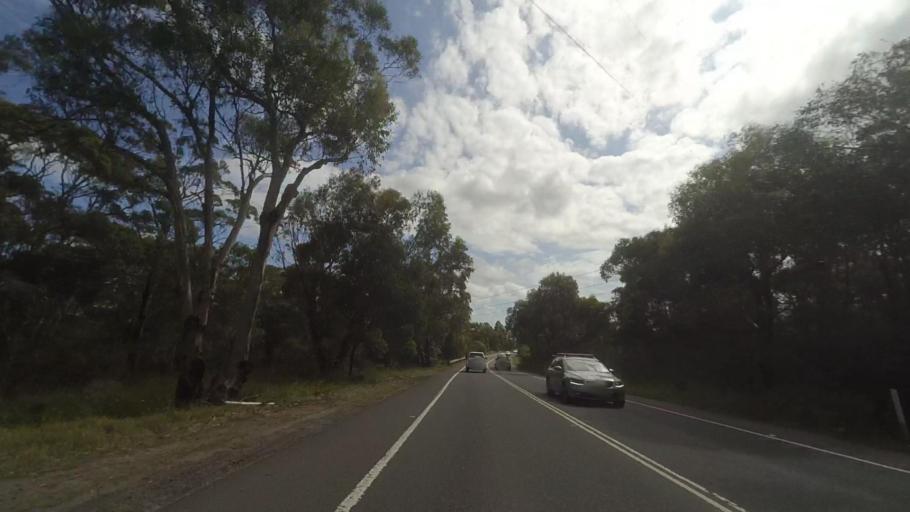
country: AU
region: New South Wales
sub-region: Sutherland Shire
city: Engadine
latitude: -34.0442
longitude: 150.9929
